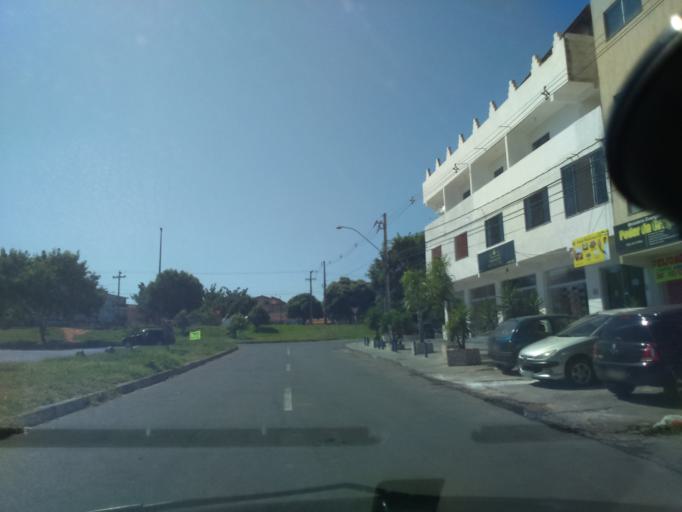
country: BR
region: Federal District
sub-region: Brasilia
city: Brasilia
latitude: -15.8490
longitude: -47.9759
